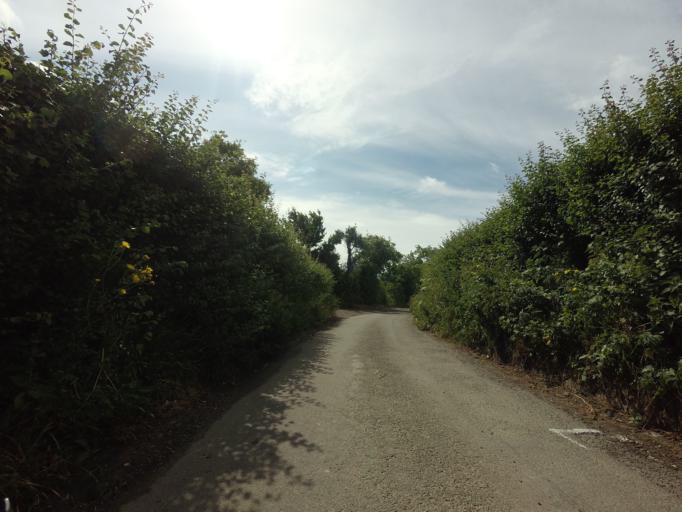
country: GB
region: England
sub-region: Kent
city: Halstead
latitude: 51.3627
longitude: 0.1319
